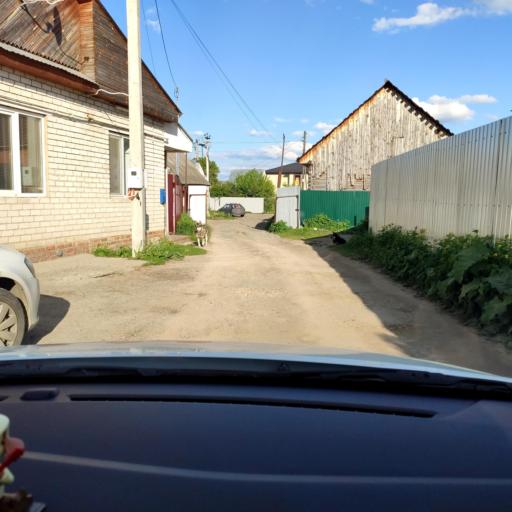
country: RU
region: Tatarstan
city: Stolbishchi
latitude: 55.7050
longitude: 49.1504
